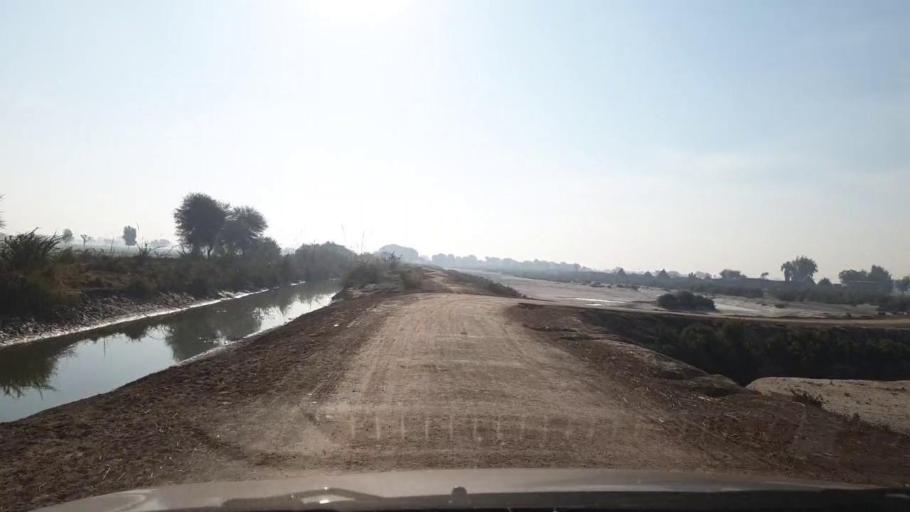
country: PK
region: Sindh
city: Jhol
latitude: 25.9359
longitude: 68.8724
